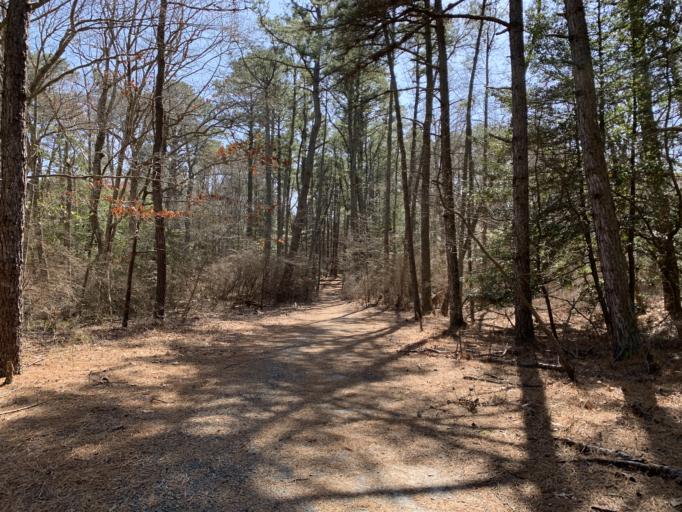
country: US
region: Delaware
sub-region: Sussex County
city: Lewes
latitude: 38.7728
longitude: -75.0897
